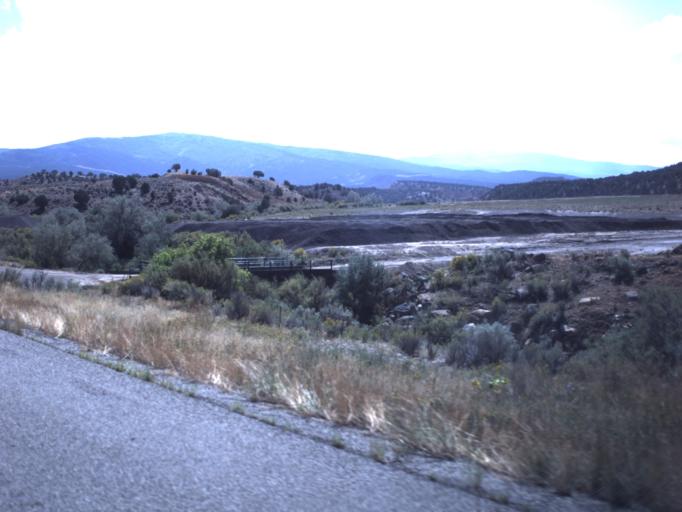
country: US
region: Utah
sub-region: Sevier County
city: Salina
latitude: 38.9196
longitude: -111.7528
